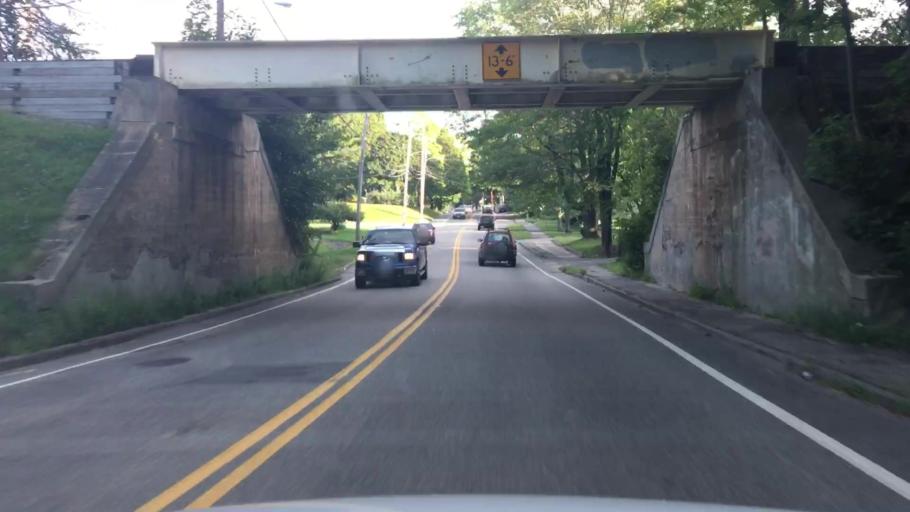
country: US
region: Maine
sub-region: Cumberland County
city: Westbrook
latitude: 43.6861
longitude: -70.3572
